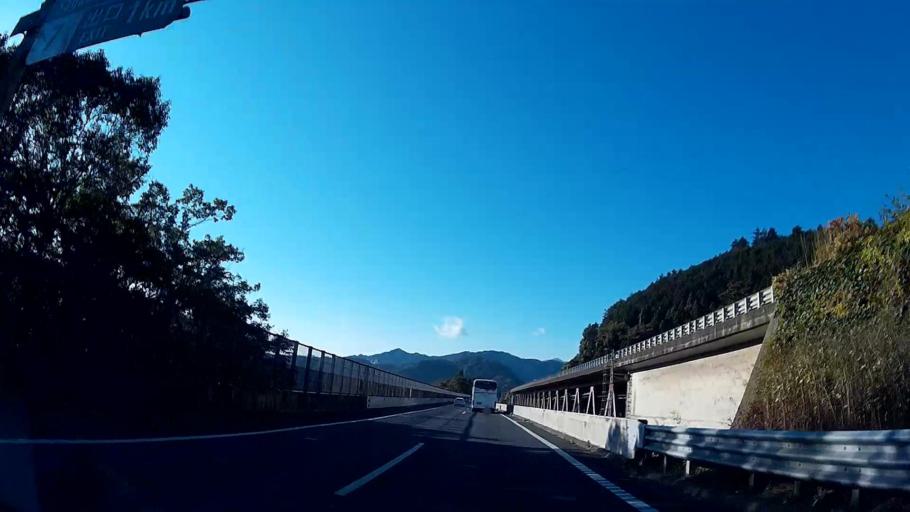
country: JP
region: Yamanashi
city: Uenohara
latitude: 35.6289
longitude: 139.2032
